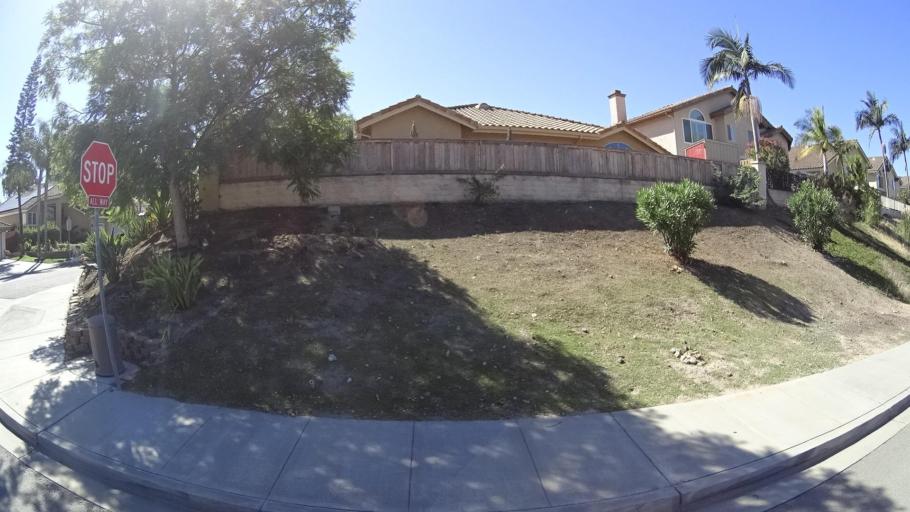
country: US
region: California
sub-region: San Diego County
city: La Presa
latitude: 32.6640
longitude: -116.9779
